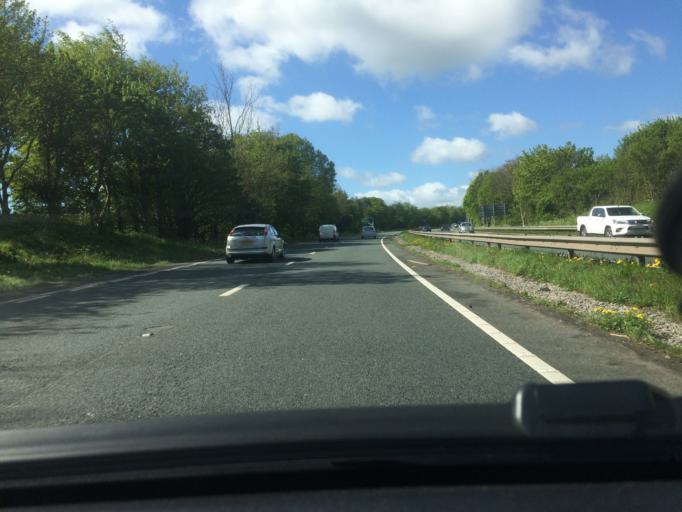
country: GB
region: Wales
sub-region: Wrexham
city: Wrexham
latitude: 53.0510
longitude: -3.0144
